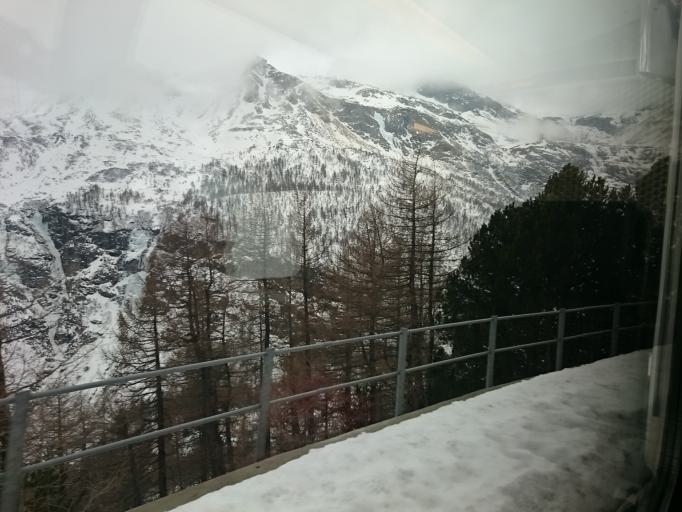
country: CH
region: Grisons
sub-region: Bernina District
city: Poschiavo
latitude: 46.3731
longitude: 10.0323
